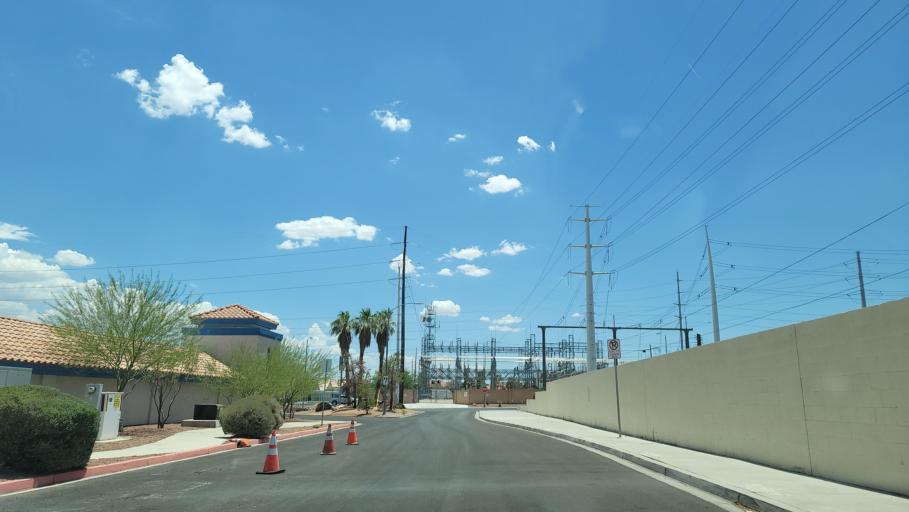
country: US
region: Nevada
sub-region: Clark County
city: Spring Valley
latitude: 36.1600
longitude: -115.2779
